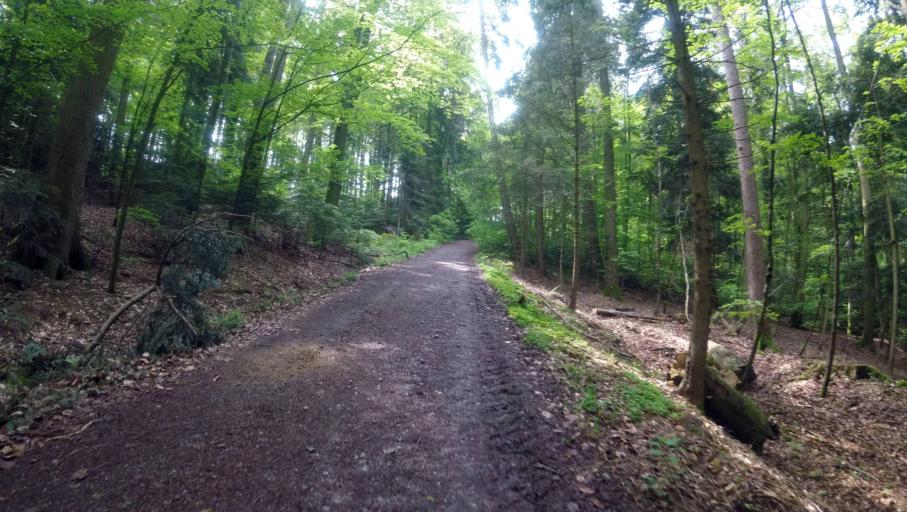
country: DE
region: Baden-Wuerttemberg
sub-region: Regierungsbezirk Stuttgart
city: Kaisersbach
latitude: 48.9176
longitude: 9.6150
